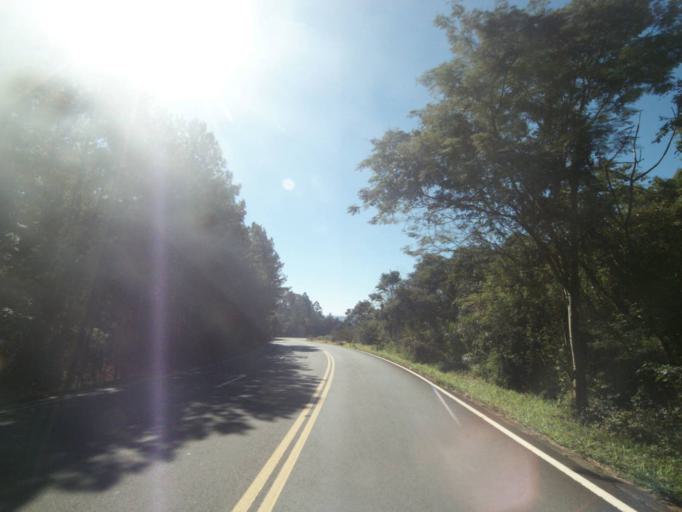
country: BR
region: Parana
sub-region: Tibagi
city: Tibagi
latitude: -24.4753
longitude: -50.5088
